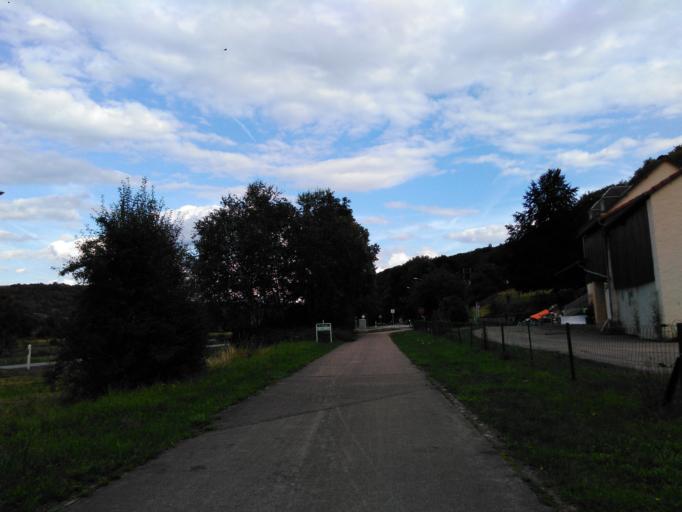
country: DE
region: Rheinland-Pfalz
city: Menningen
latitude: 49.8149
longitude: 6.4806
